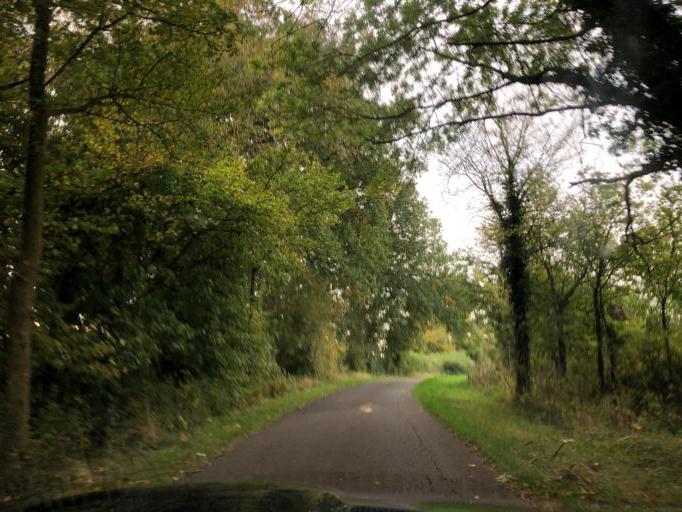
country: GB
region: England
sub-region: Warwickshire
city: Wroxall
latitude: 52.3272
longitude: -1.6524
